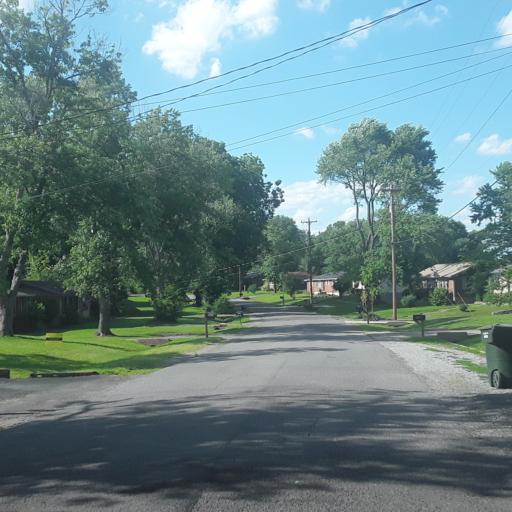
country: US
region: Tennessee
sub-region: Davidson County
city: Lakewood
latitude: 36.2054
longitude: -86.6358
